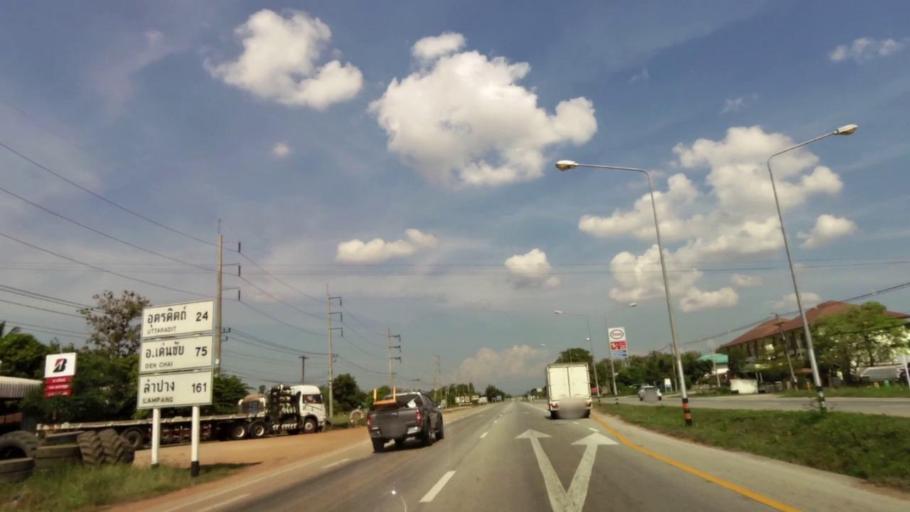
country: TH
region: Uttaradit
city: Thong Saen Khan
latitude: 17.4743
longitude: 100.2358
